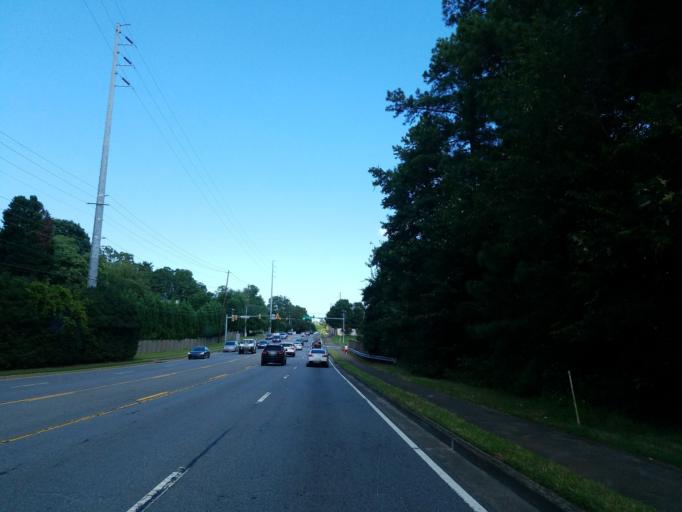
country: US
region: Georgia
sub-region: Fulton County
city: Roswell
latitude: 34.0335
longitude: -84.4429
